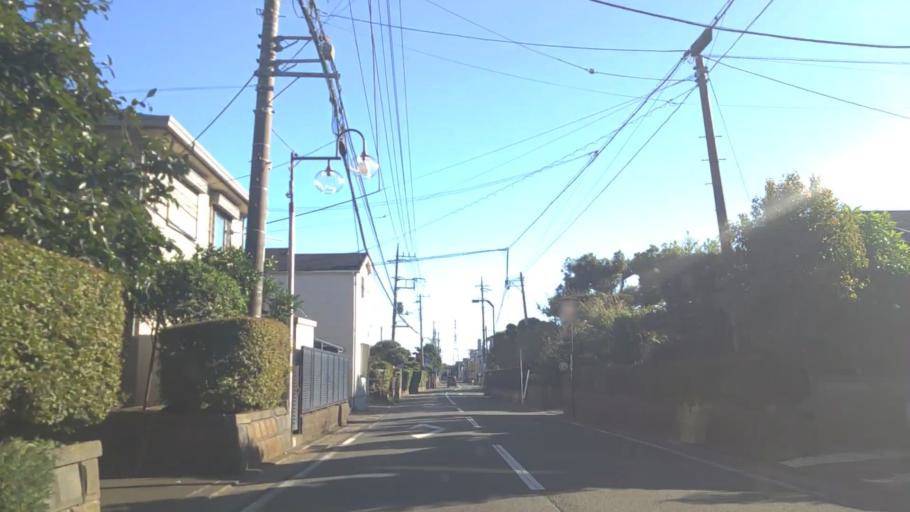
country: JP
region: Kanagawa
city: Isehara
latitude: 35.3794
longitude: 139.3649
